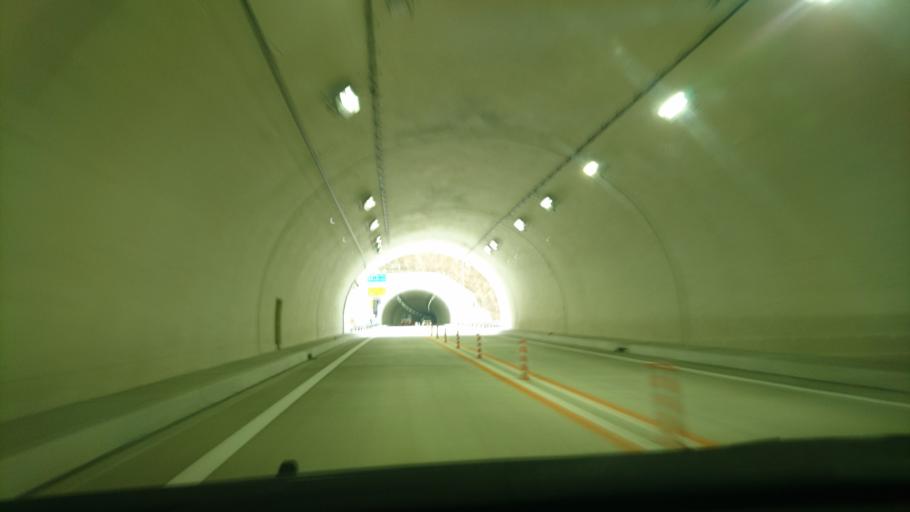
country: JP
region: Iwate
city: Kamaishi
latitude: 39.2864
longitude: 141.8628
